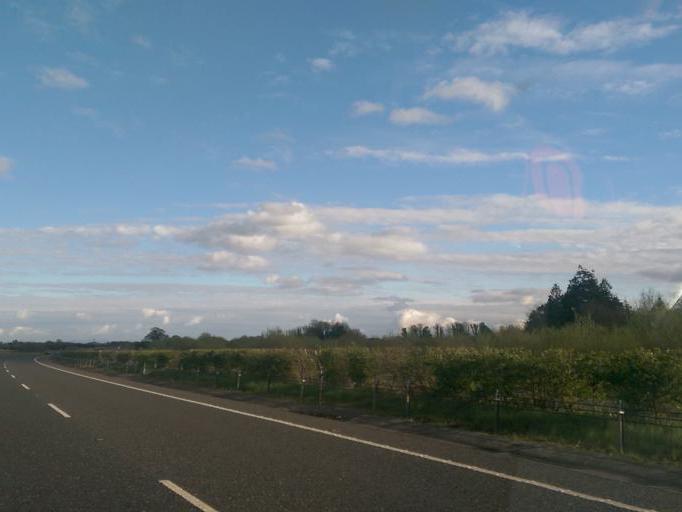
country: IE
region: Leinster
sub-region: An Mhi
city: Longwood
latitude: 53.4231
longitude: -6.9149
